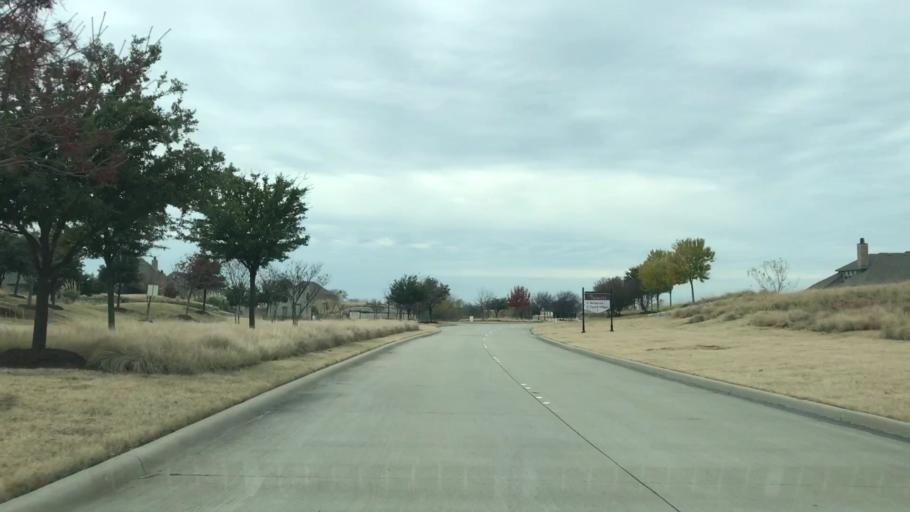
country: US
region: Texas
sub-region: Denton County
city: The Colony
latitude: 33.1083
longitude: -96.9205
